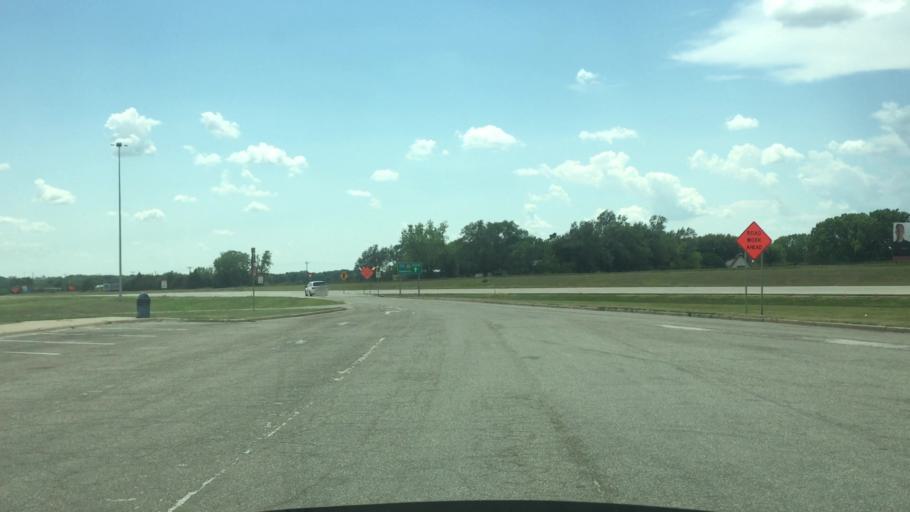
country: US
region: Kansas
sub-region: Lyon County
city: Emporia
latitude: 38.4703
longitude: -96.1862
